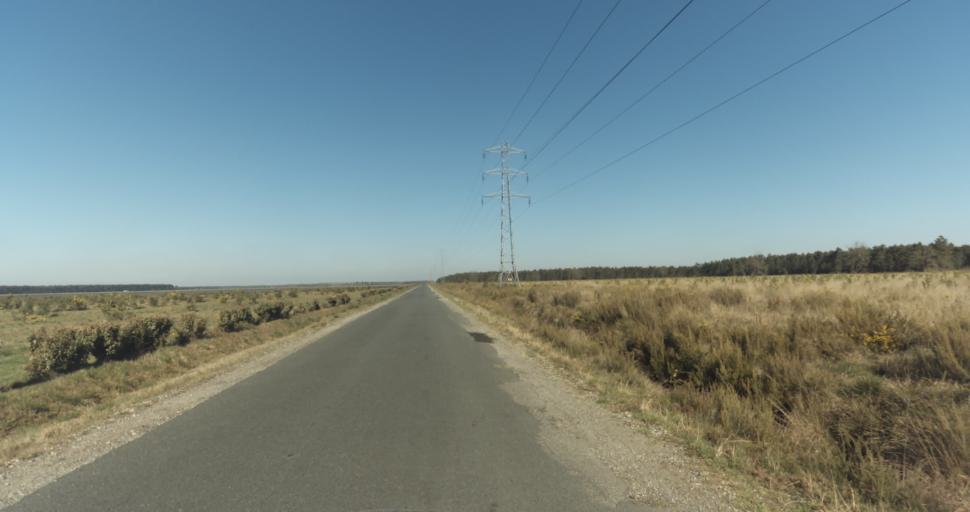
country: FR
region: Aquitaine
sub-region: Departement de la Gironde
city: Marcheprime
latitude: 44.7408
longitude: -0.8220
